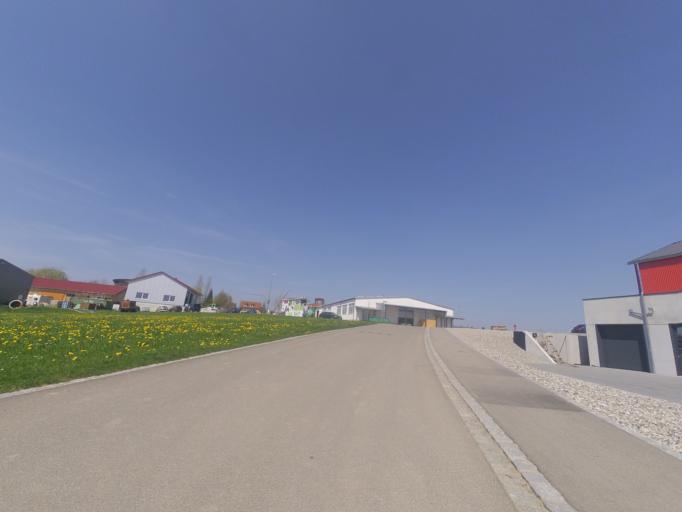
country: DE
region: Bavaria
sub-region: Swabia
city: Roggenburg
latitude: 48.2859
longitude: 10.2095
